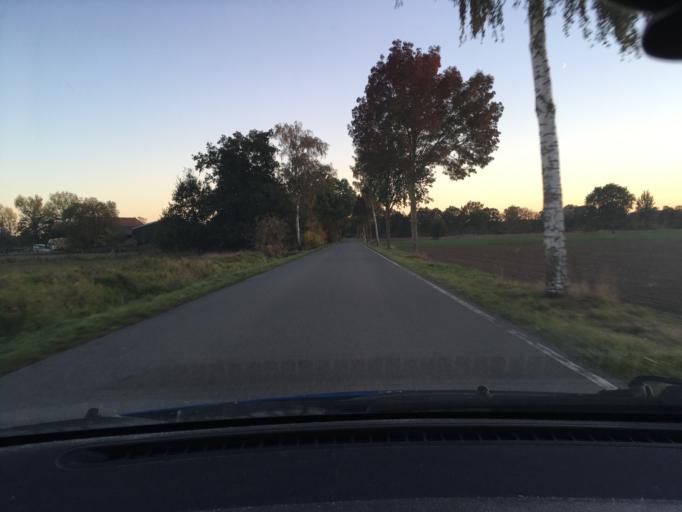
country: DE
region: Lower Saxony
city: Neetze
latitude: 53.3053
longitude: 10.6164
